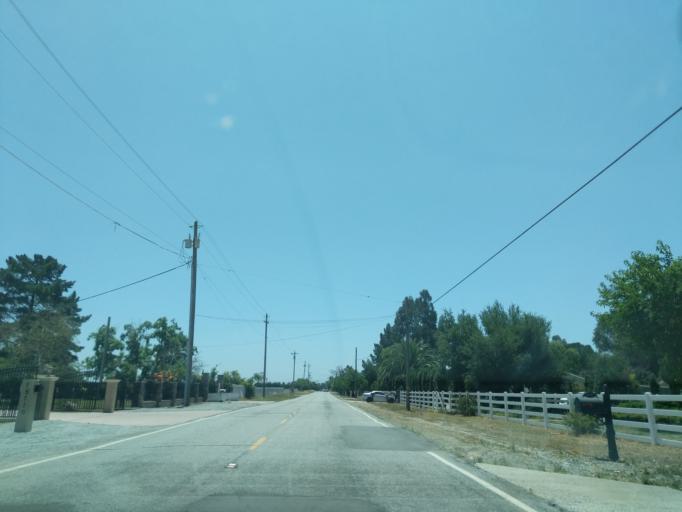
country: US
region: California
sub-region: Santa Clara County
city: San Martin
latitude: 37.1102
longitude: -121.6148
